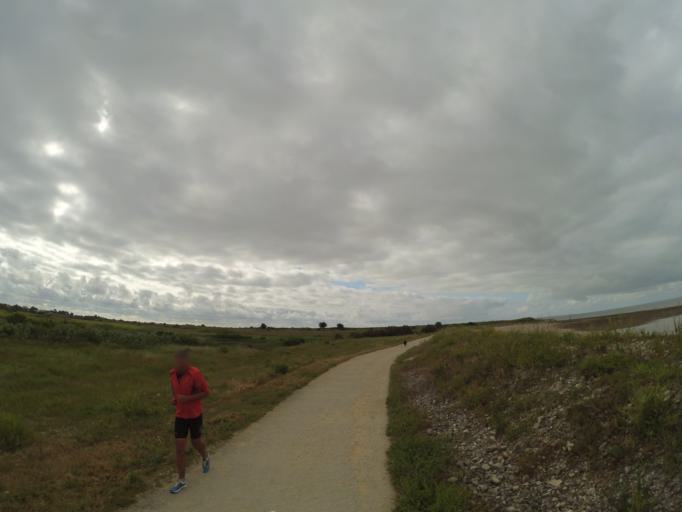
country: FR
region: Poitou-Charentes
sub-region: Departement de la Charente-Maritime
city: La Rochelle
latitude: 46.1327
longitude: -1.1486
